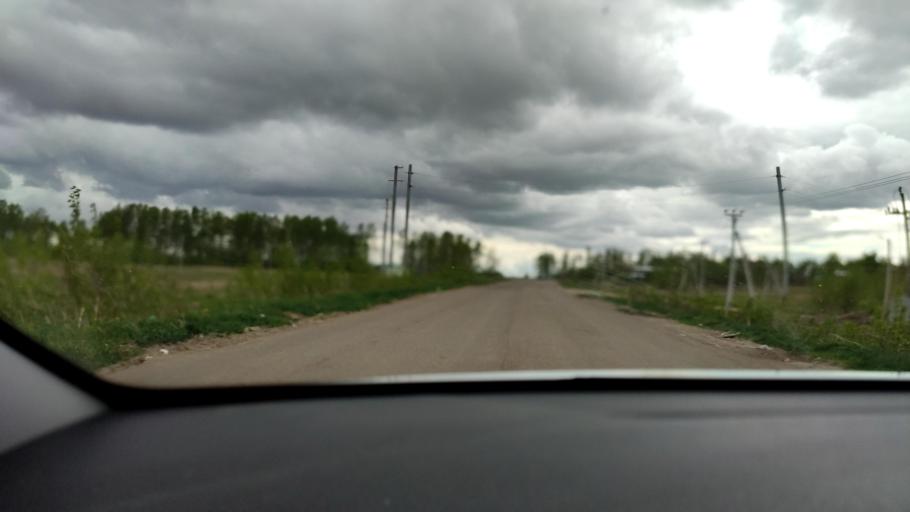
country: RU
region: Tatarstan
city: Vysokaya Gora
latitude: 55.8035
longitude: 49.3135
